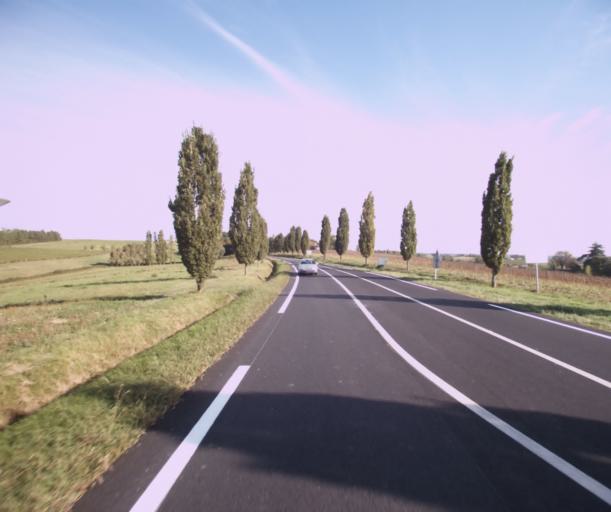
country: FR
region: Midi-Pyrenees
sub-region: Departement du Gers
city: Eauze
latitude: 43.8597
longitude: 0.0622
